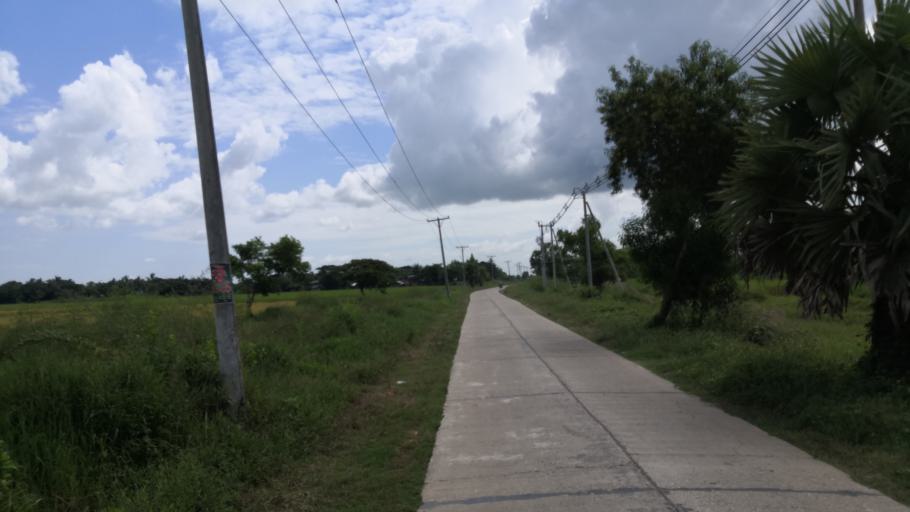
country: MM
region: Yangon
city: Kanbe
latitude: 16.4369
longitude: 96.1588
